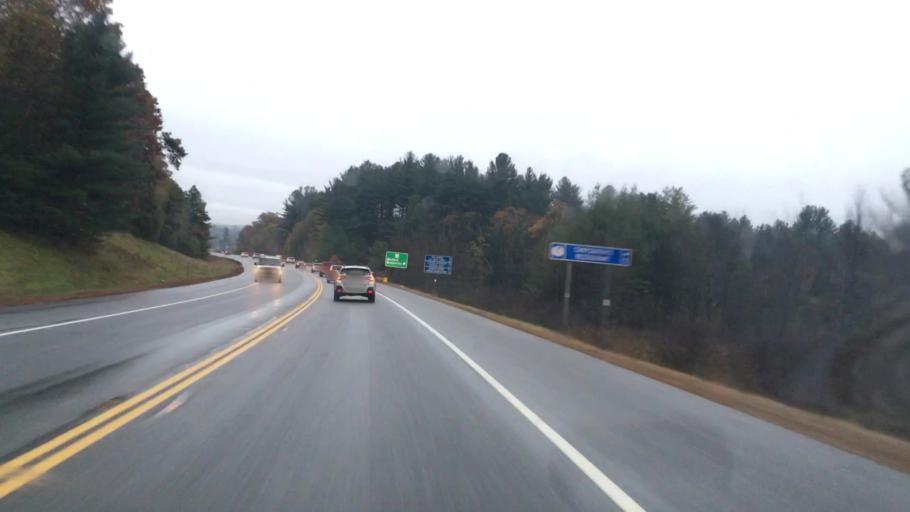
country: US
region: New Hampshire
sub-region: Hillsborough County
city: Milford
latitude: 42.8191
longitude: -71.6547
